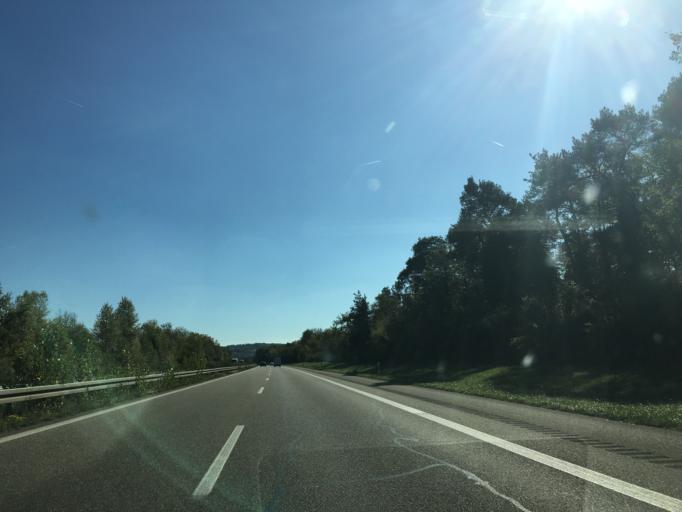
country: FR
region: Alsace
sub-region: Departement du Haut-Rhin
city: Ottmarsheim
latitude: 47.7649
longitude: 7.5391
